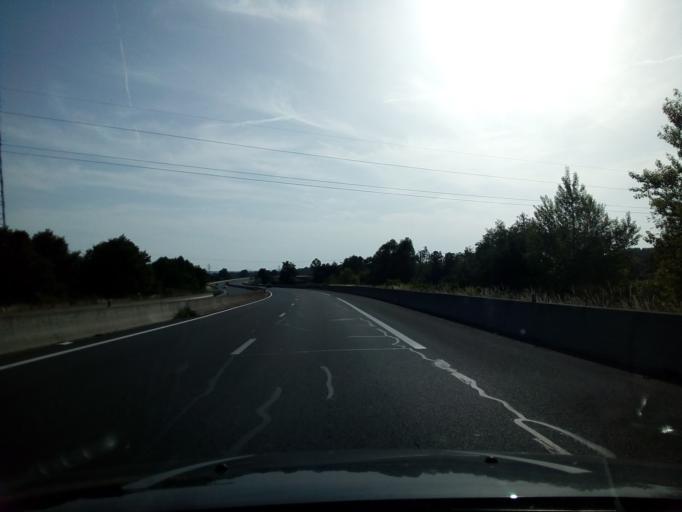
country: FR
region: Auvergne
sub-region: Departement de l'Allier
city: Saint-Victor
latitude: 46.3780
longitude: 2.6016
